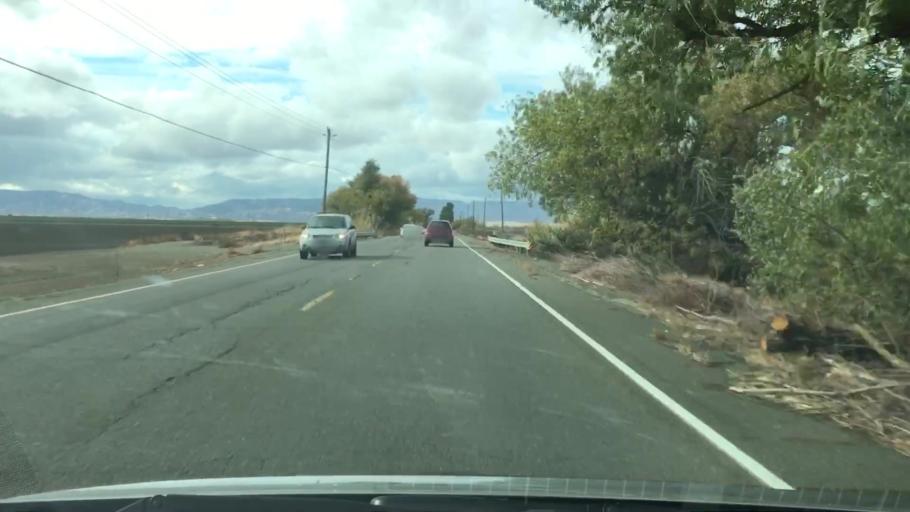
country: US
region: California
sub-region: Yolo County
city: Winters
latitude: 38.5617
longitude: -121.8715
